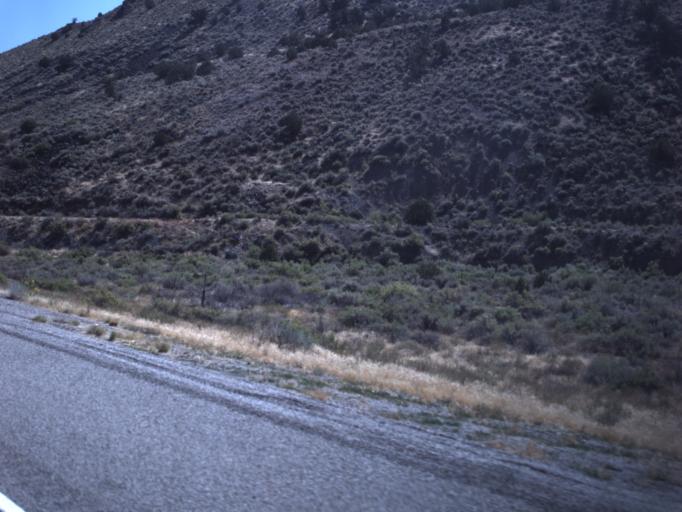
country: US
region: Utah
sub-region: Sevier County
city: Salina
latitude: 38.9302
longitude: -111.8297
